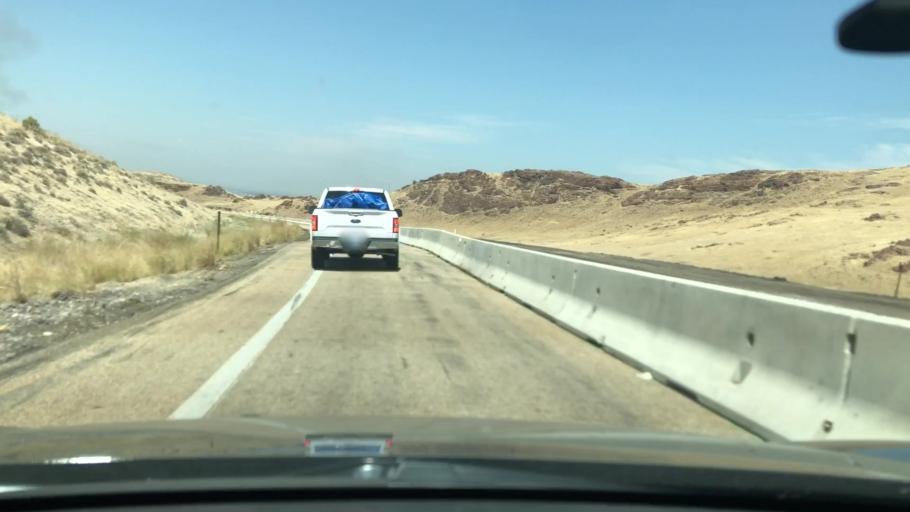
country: US
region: Idaho
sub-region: Owyhee County
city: Marsing
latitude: 43.4522
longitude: -116.8608
